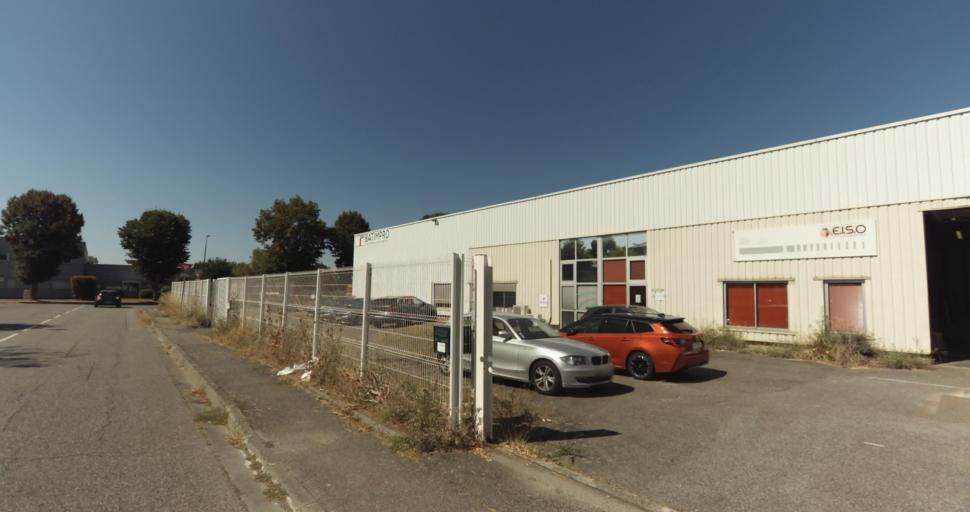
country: FR
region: Midi-Pyrenees
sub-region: Departement de la Haute-Garonne
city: Saint-Jean
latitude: 43.6399
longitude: 1.4971
